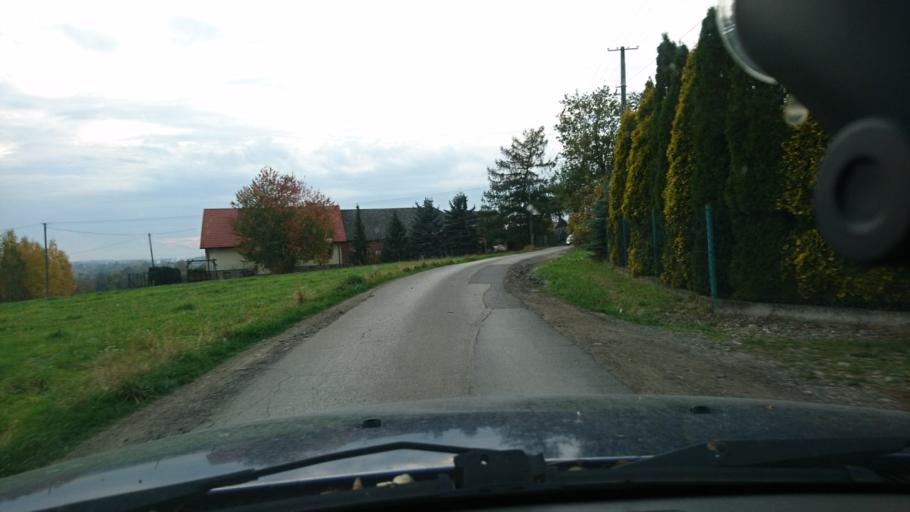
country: PL
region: Silesian Voivodeship
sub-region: Powiat bielski
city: Kozy
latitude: 49.8655
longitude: 19.1559
